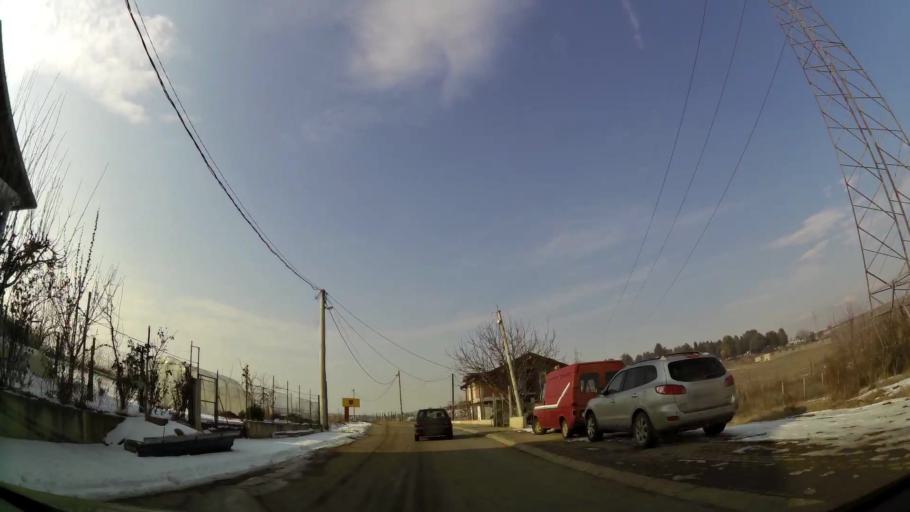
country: MK
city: Creshevo
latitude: 42.0133
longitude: 21.4948
